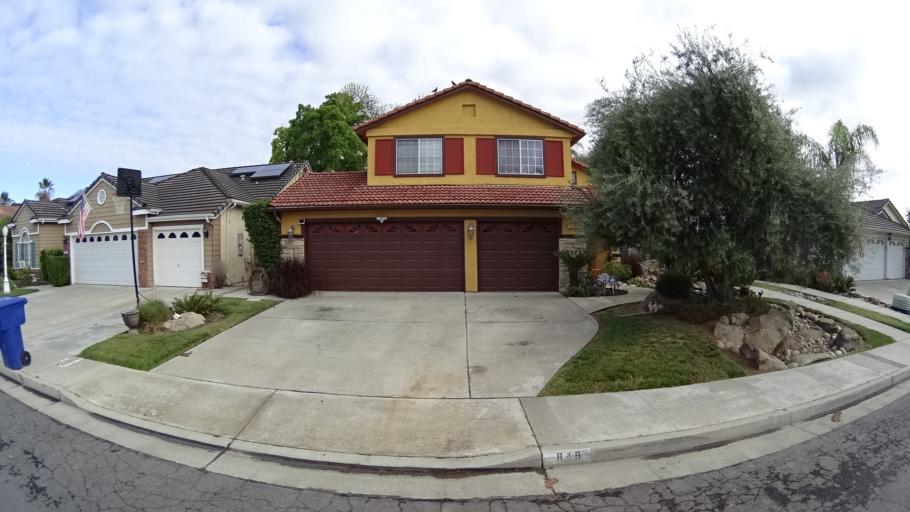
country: US
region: California
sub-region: Kings County
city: Hanford
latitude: 36.3594
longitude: -119.6338
